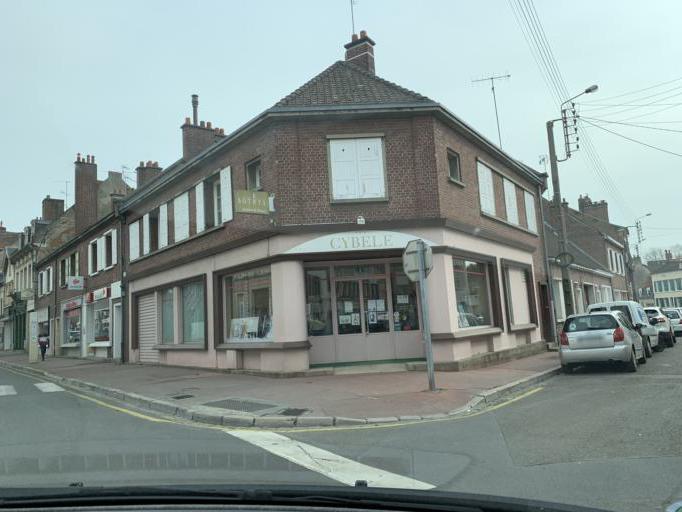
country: FR
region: Picardie
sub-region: Departement de la Somme
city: Abbeville
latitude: 50.1095
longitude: 1.8306
